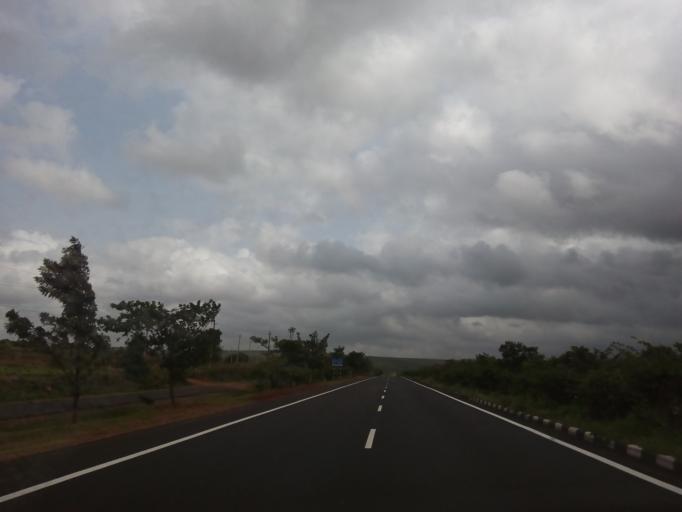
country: IN
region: Karnataka
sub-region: Belgaum
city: Hukeri
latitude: 16.0851
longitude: 74.5183
